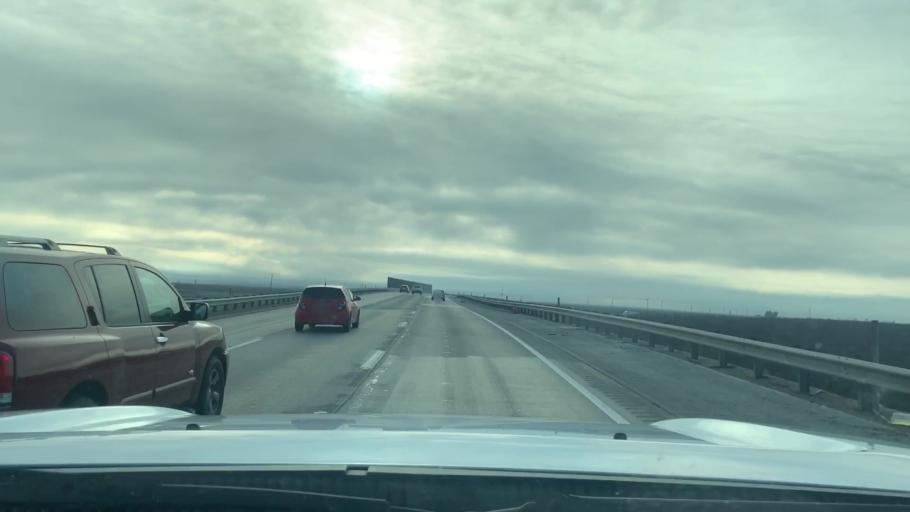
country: US
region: California
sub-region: Kern County
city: McFarland
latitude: 35.5926
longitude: -119.2080
